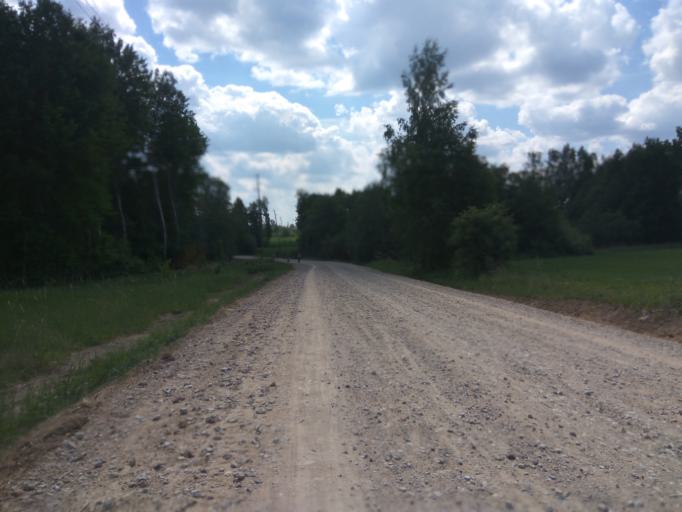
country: LV
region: Kuldigas Rajons
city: Kuldiga
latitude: 56.9079
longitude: 21.9637
